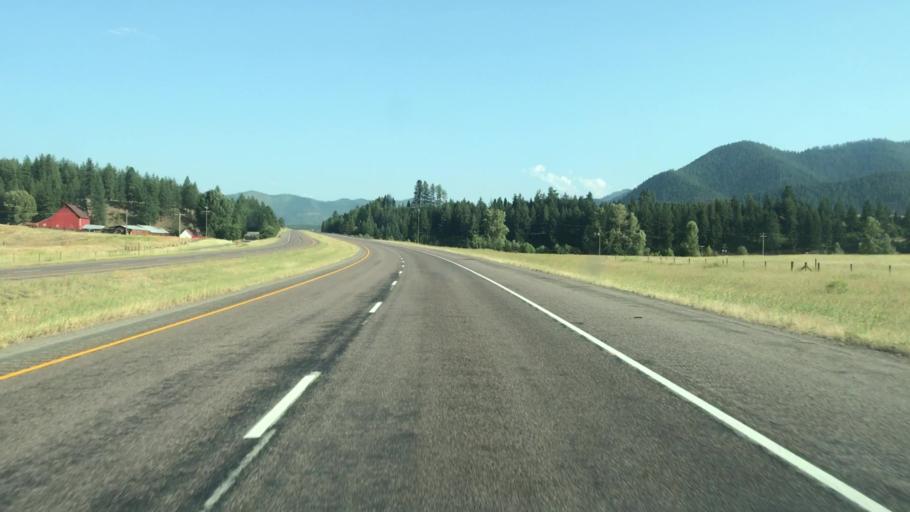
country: US
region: Montana
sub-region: Mineral County
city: Superior
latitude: 47.0572
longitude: -114.7620
